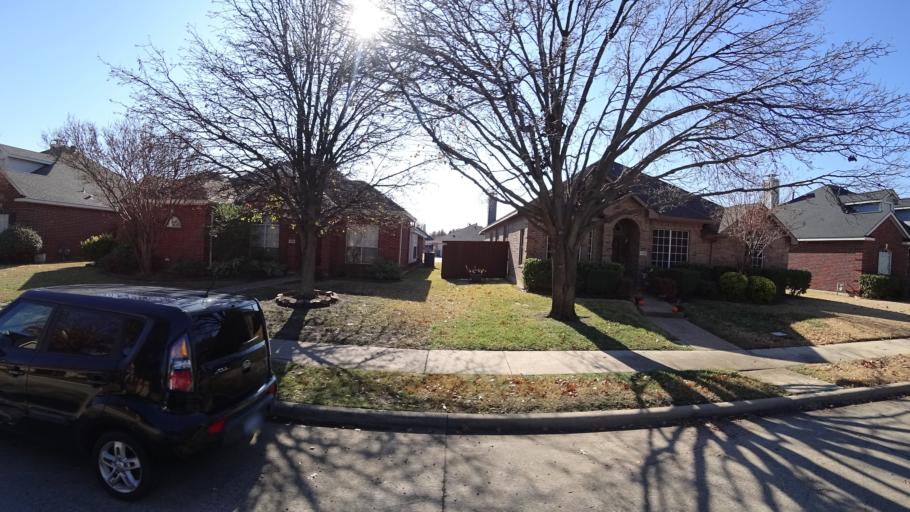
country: US
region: Texas
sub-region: Denton County
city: Lewisville
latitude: 33.0104
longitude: -97.0234
